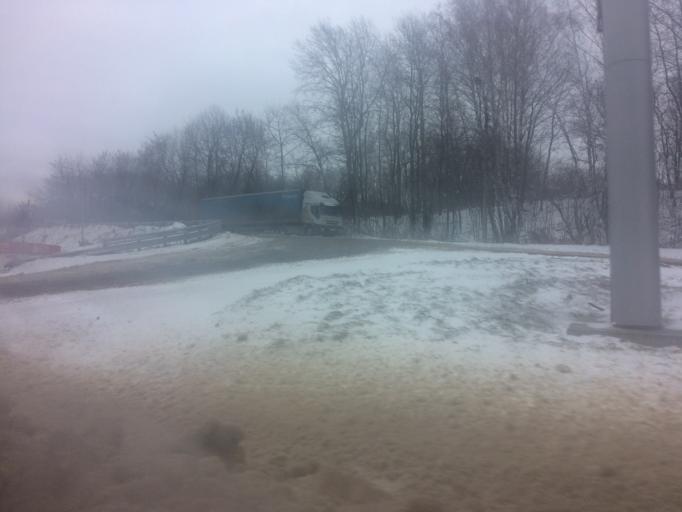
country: RU
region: Tula
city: Tula
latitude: 54.1667
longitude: 37.6310
